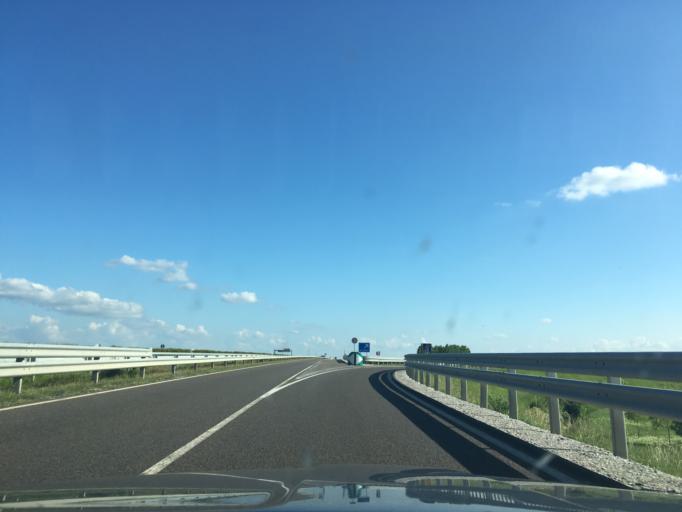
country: HU
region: Hajdu-Bihar
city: Debrecen
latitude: 47.5534
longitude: 21.5510
